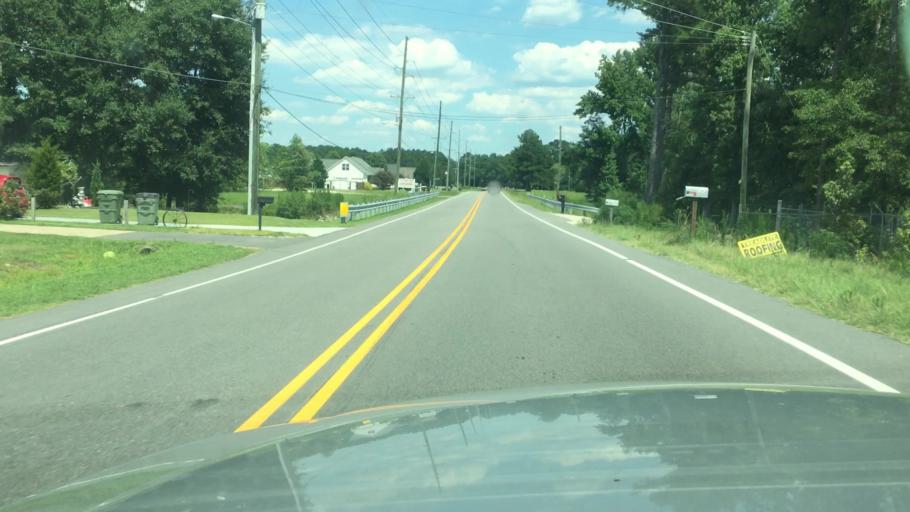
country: US
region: North Carolina
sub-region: Cumberland County
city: Hope Mills
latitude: 34.9468
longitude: -78.8730
